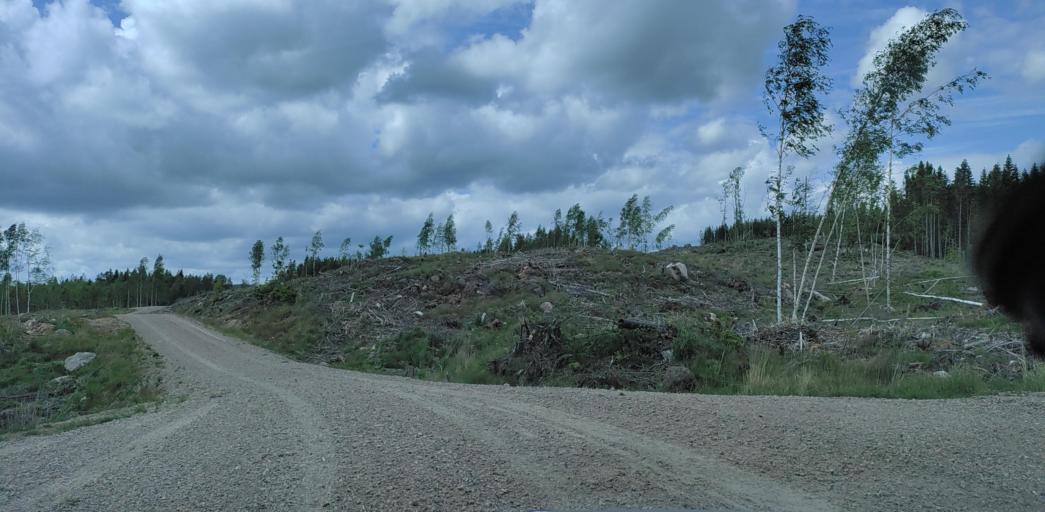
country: SE
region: Vaermland
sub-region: Munkfors Kommun
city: Munkfors
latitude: 59.9459
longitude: 13.4233
